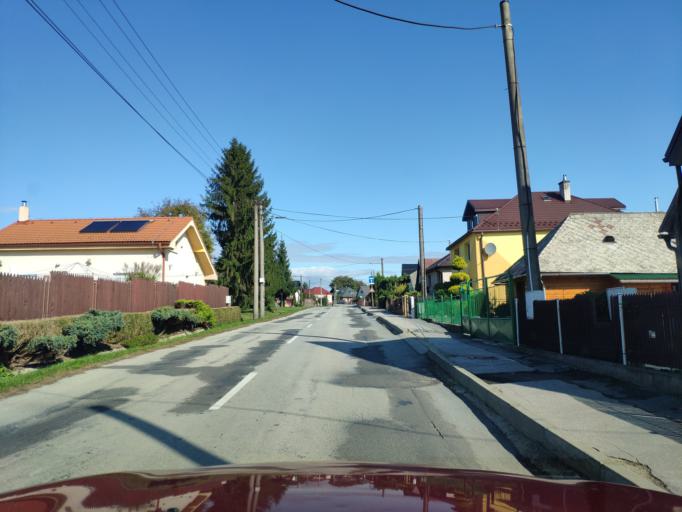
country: SK
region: Presovsky
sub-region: Okres Presov
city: Presov
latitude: 48.8749
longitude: 21.2700
